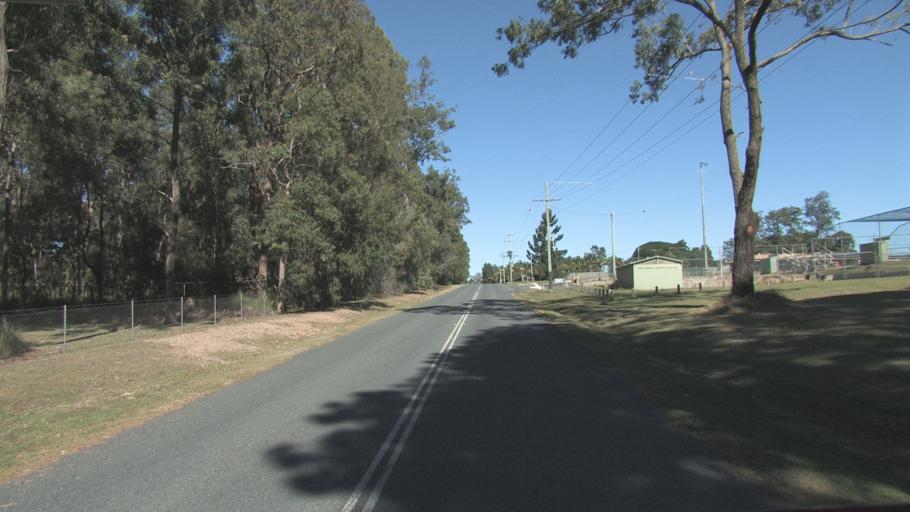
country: AU
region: Queensland
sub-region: Logan
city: Park Ridge South
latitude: -27.7049
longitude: 153.0587
